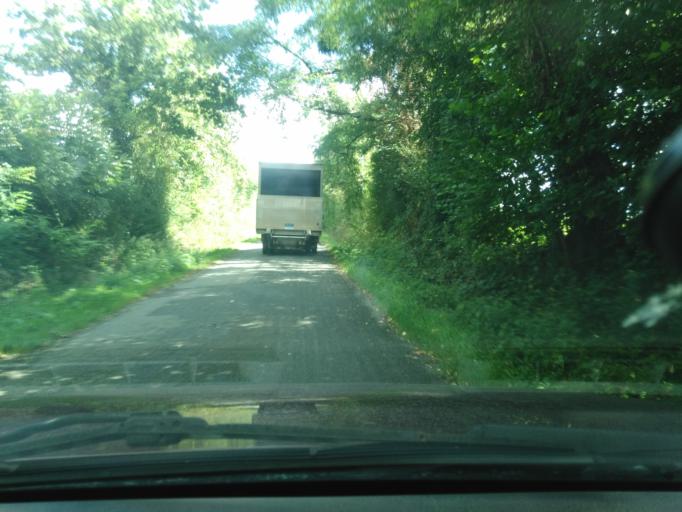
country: FR
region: Pays de la Loire
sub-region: Departement de la Vendee
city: Dompierre-sur-Yon
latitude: 46.7421
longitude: -1.3523
